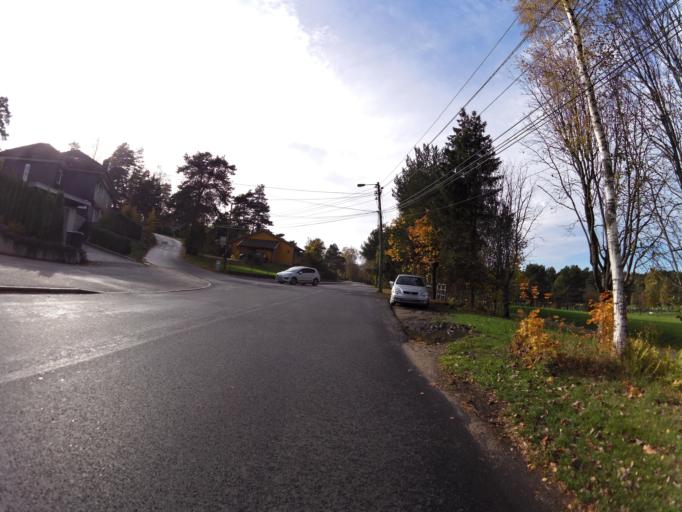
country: NO
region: Ostfold
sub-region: Fredrikstad
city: Fredrikstad
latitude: 59.2287
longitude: 10.9629
